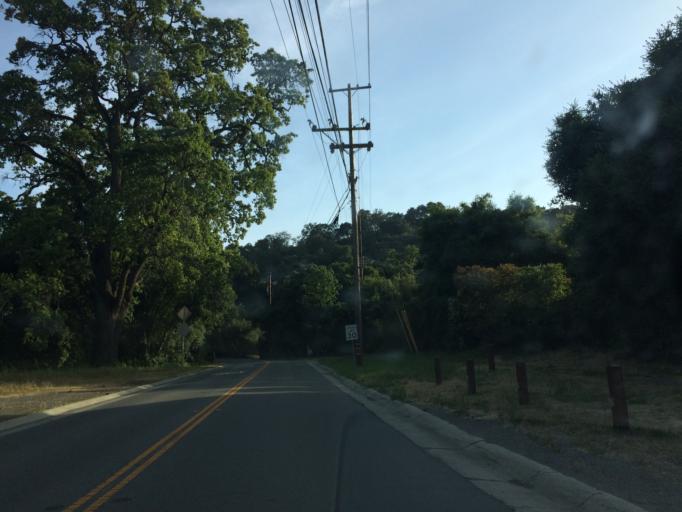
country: US
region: California
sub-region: Santa Clara County
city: Los Altos Hills
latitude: 37.3849
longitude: -122.1657
